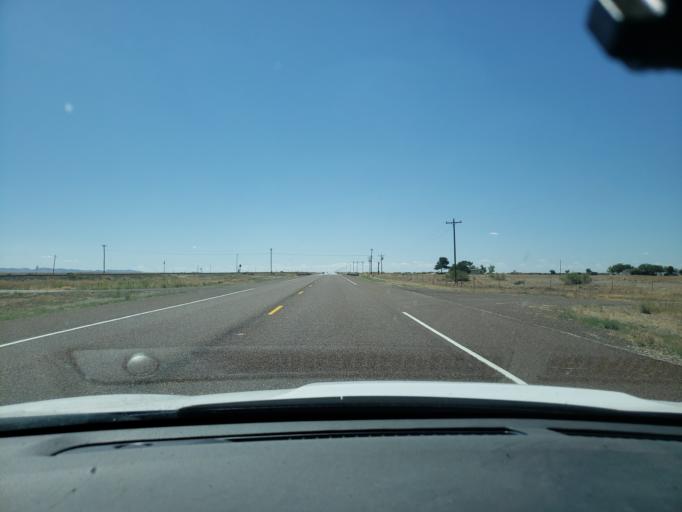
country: US
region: Texas
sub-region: Presidio County
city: Marfa
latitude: 30.5401
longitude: -104.4381
